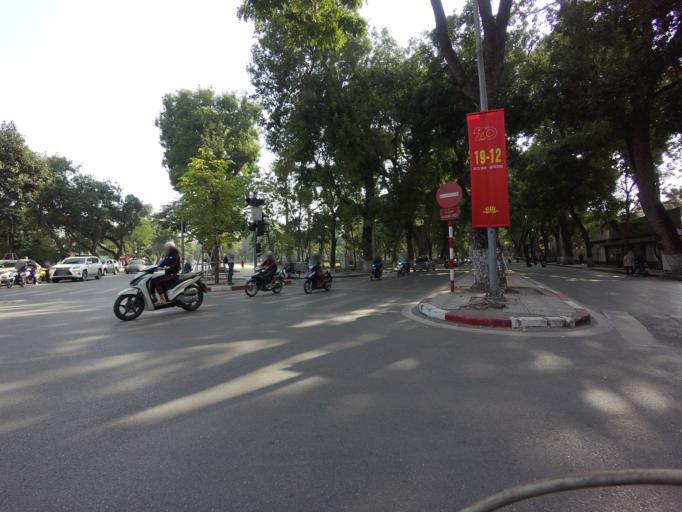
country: VN
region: Ha Noi
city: Hanoi
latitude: 21.0328
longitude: 105.8389
